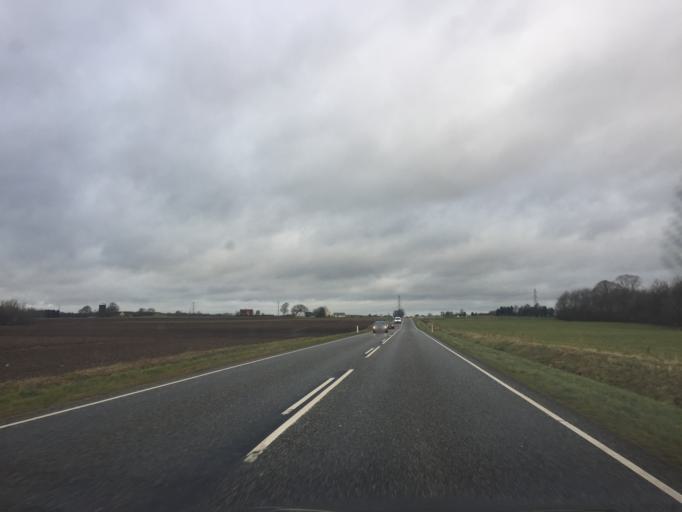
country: DK
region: Zealand
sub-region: Soro Kommune
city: Soro
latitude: 55.4864
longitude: 11.5719
